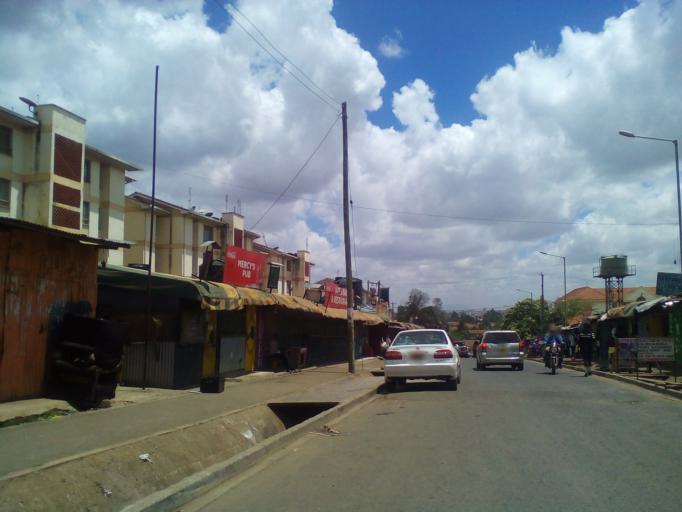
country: KE
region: Nairobi Area
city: Nairobi
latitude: -1.3148
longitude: 36.8056
